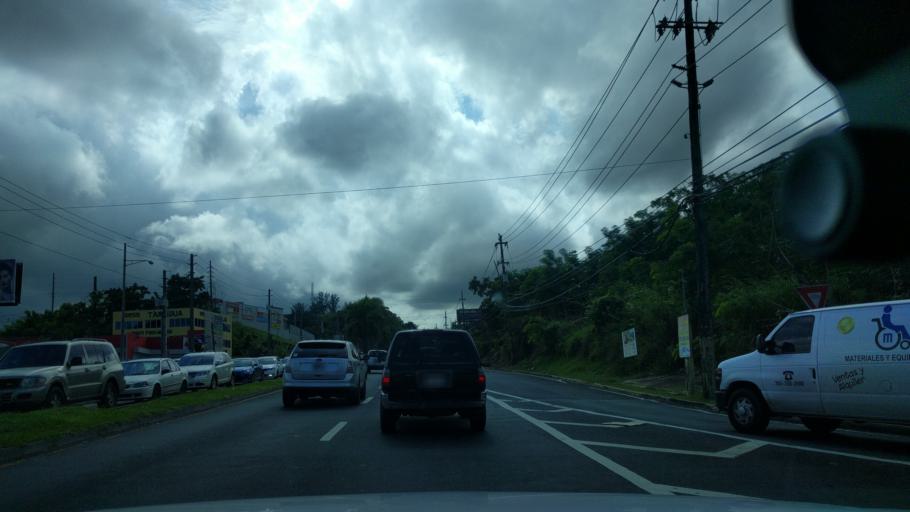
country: PR
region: Toa Alta
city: Pajaros
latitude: 18.3645
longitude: -66.1887
